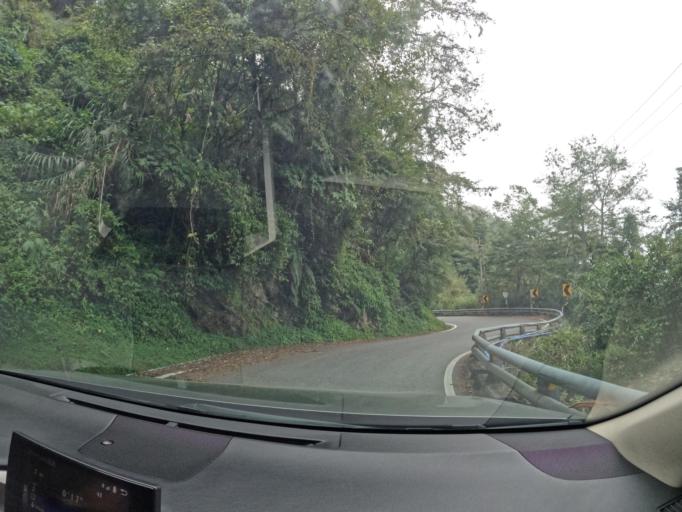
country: TW
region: Taiwan
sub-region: Taitung
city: Taitung
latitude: 23.2448
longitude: 120.9962
